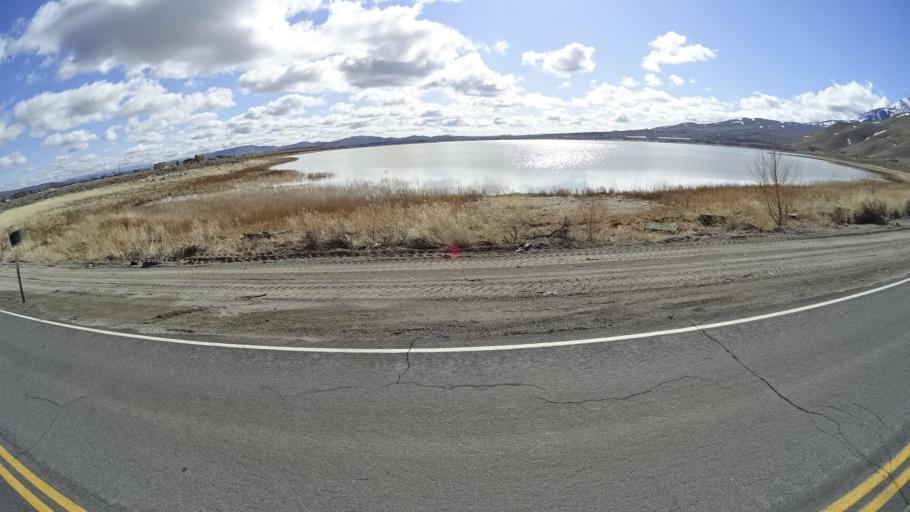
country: US
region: Nevada
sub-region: Washoe County
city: Cold Springs
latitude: 39.6507
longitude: -119.9272
